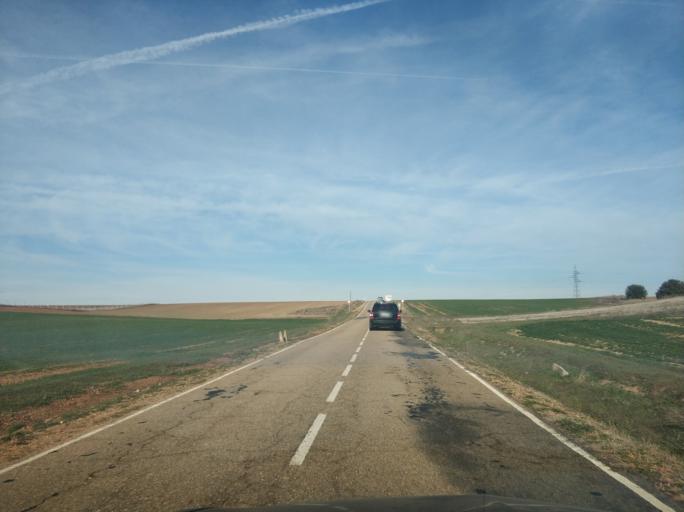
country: ES
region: Castille and Leon
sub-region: Provincia de Salamanca
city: Parada de Arriba
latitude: 40.9923
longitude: -5.8056
